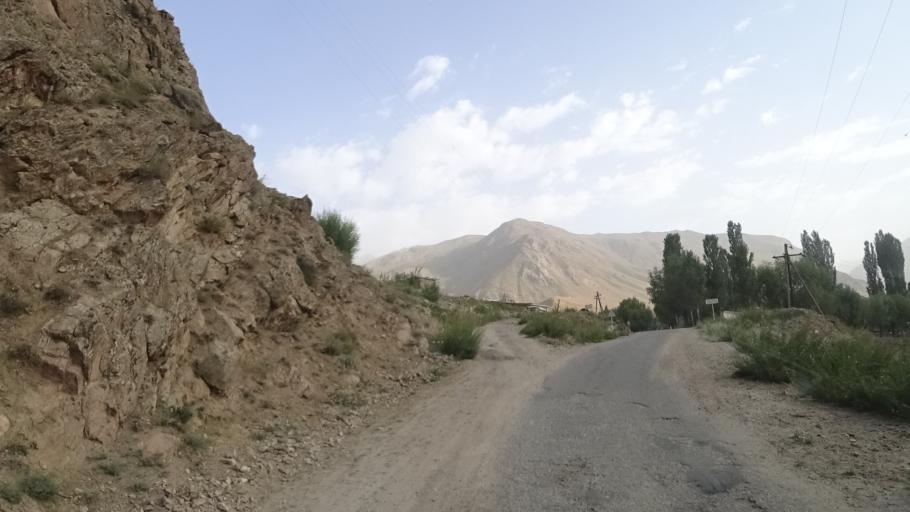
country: TJ
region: Gorno-Badakhshan
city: Khorugh
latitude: 37.2389
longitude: 71.4847
